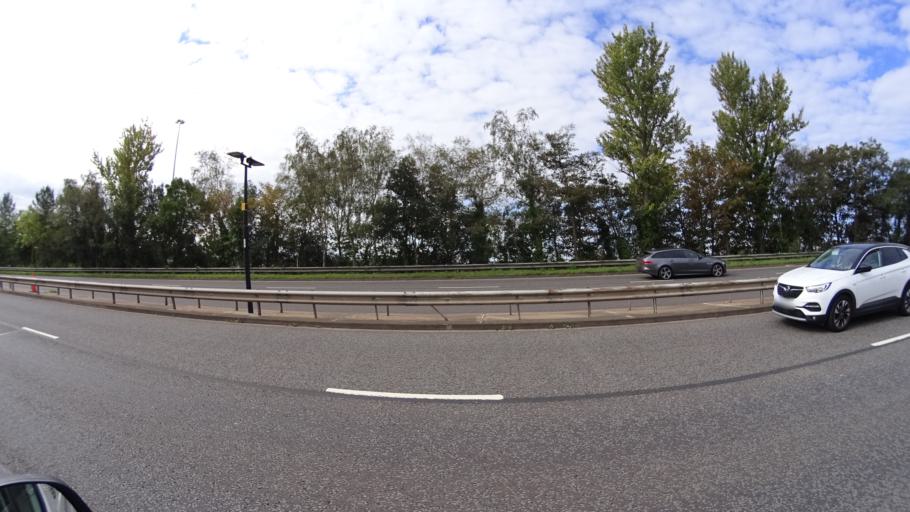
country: GB
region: England
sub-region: Southampton
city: Southampton
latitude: 50.9095
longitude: -1.4293
